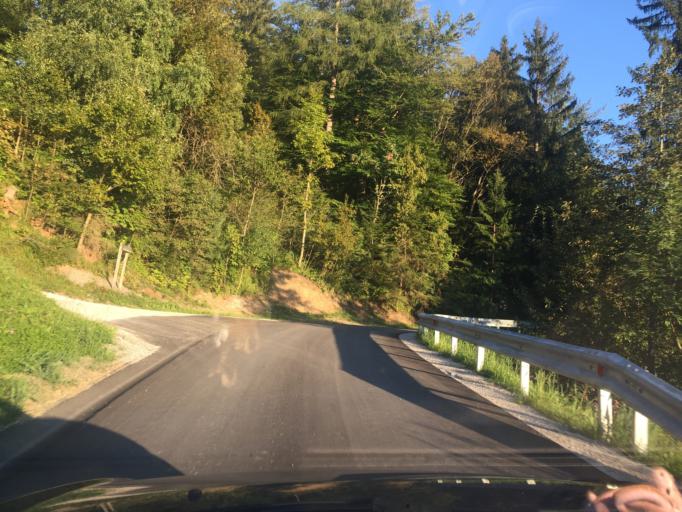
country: SI
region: Sostanj
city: Topolsica
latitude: 46.4517
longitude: 14.9960
